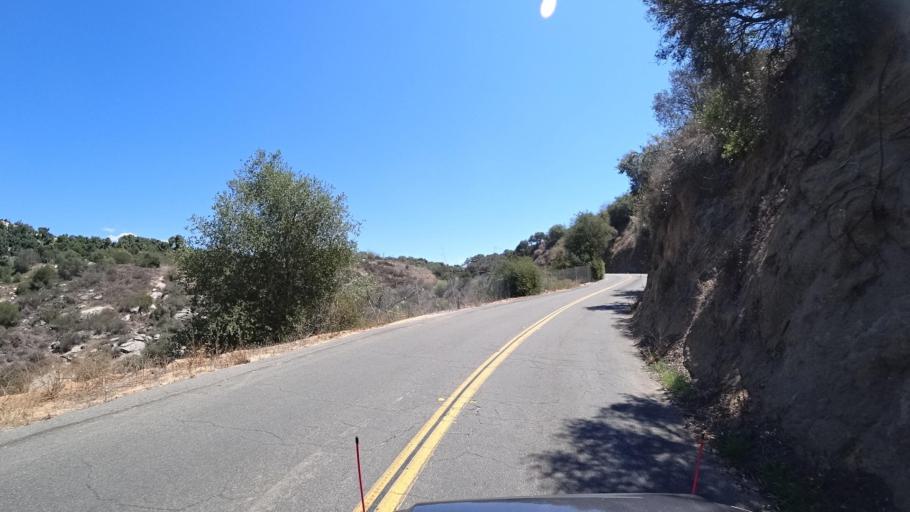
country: US
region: California
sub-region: San Diego County
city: Hidden Meadows
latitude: 33.3090
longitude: -117.0949
